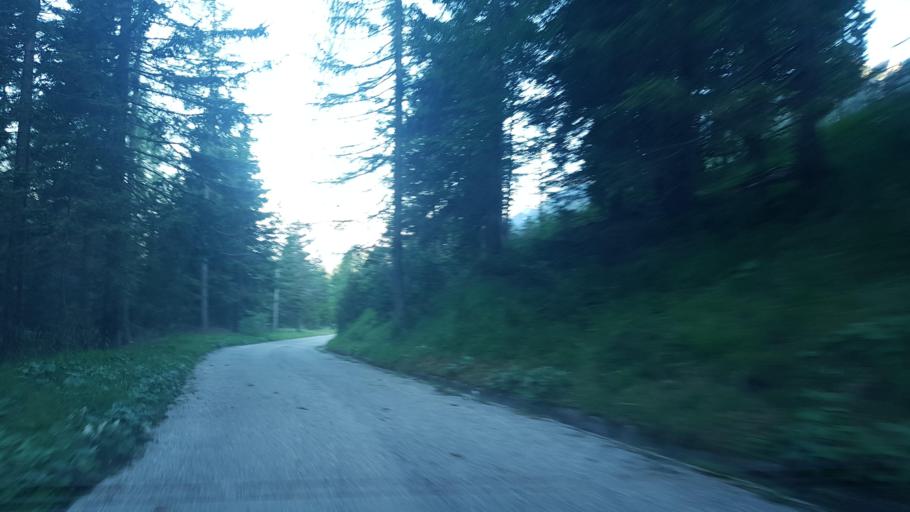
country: IT
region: Friuli Venezia Giulia
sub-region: Provincia di Udine
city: Malborghetto
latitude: 46.4632
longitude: 13.4400
